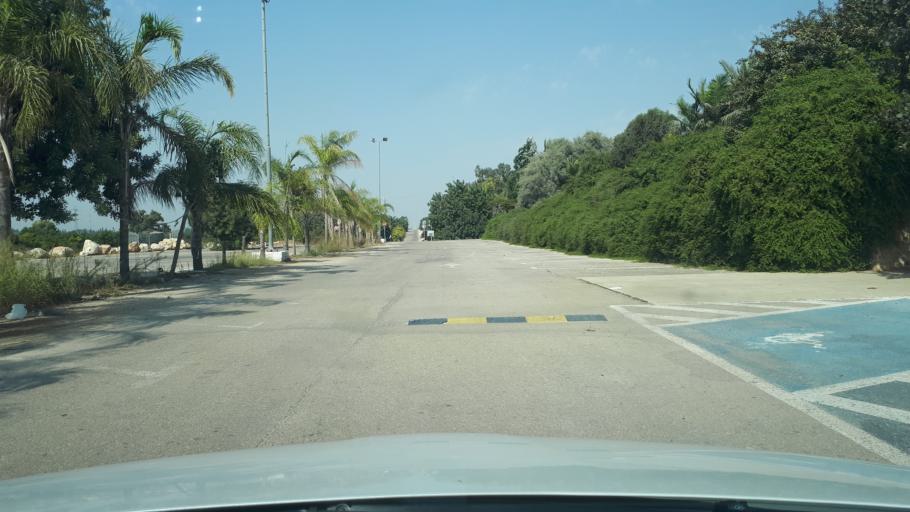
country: IL
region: Central District
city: Nehalim
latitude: 32.0612
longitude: 34.9457
